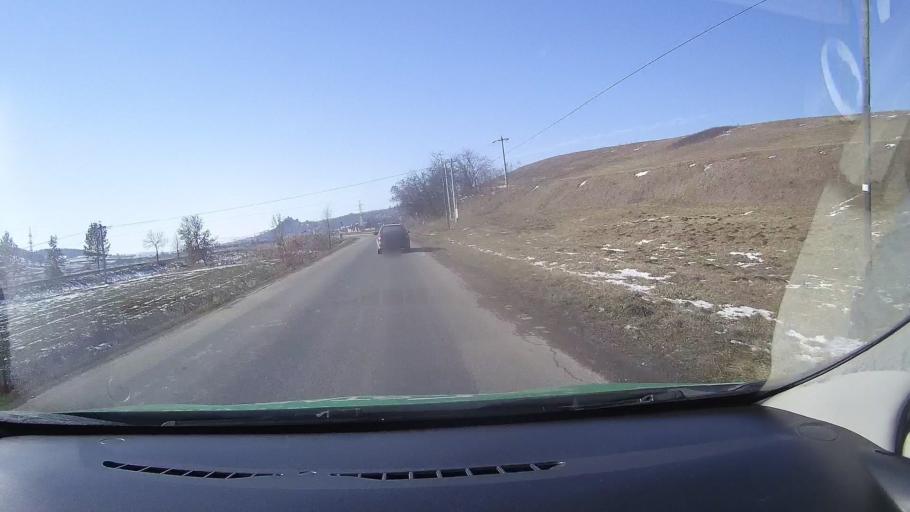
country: RO
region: Brasov
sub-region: Comuna Homorod
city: Homorod
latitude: 46.0403
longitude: 25.2464
